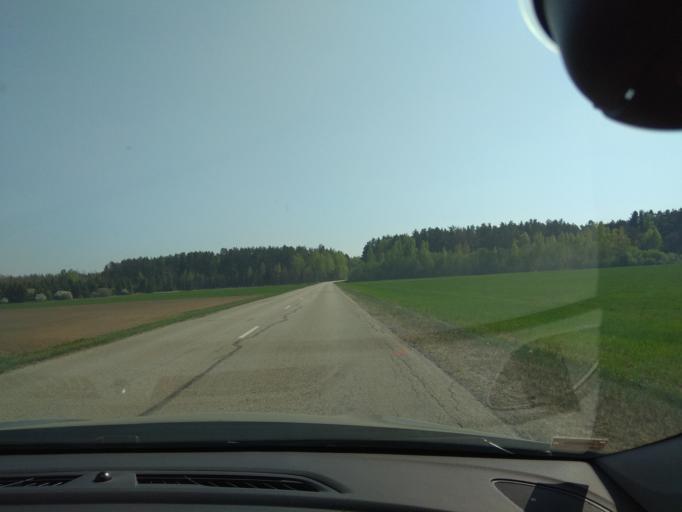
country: LT
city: Linkuva
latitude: 55.9986
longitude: 24.1673
